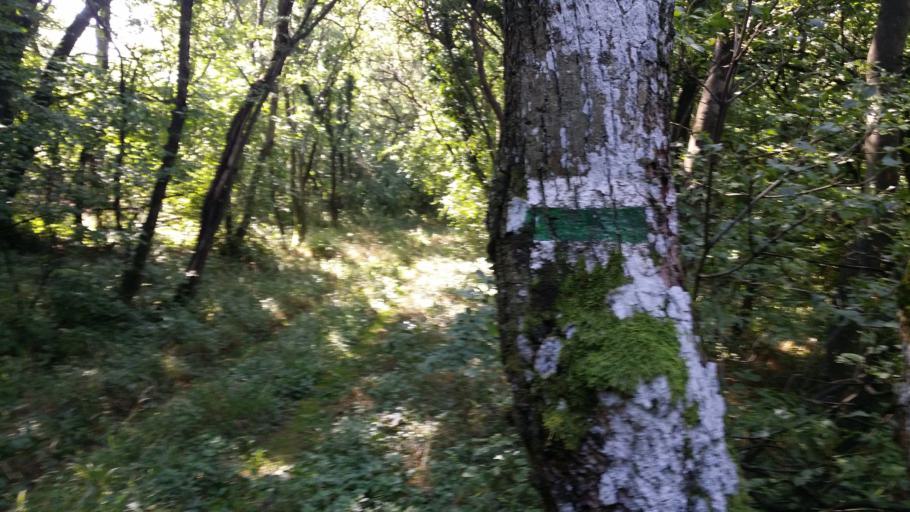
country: HU
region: Baranya
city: Pecs
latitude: 46.1121
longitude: 18.1958
